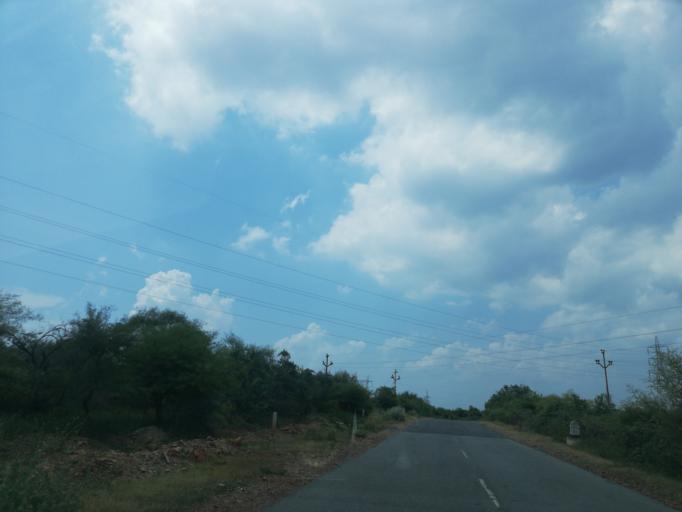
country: IN
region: Andhra Pradesh
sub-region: Guntur
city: Macherla
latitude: 16.5639
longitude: 79.3496
